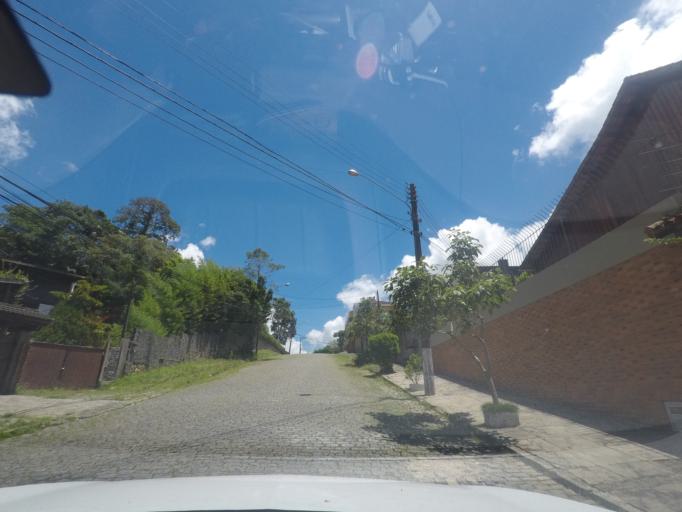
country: BR
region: Rio de Janeiro
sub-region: Teresopolis
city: Teresopolis
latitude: -22.4340
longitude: -42.9820
